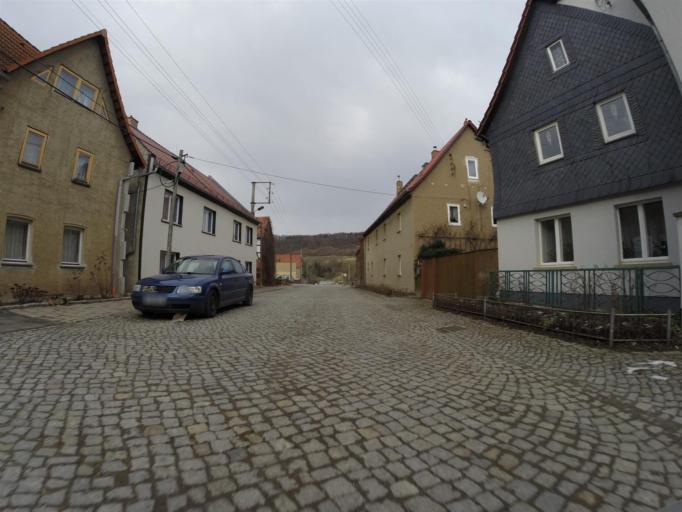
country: DE
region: Thuringia
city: Grosslobichau
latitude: 50.9283
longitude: 11.6783
